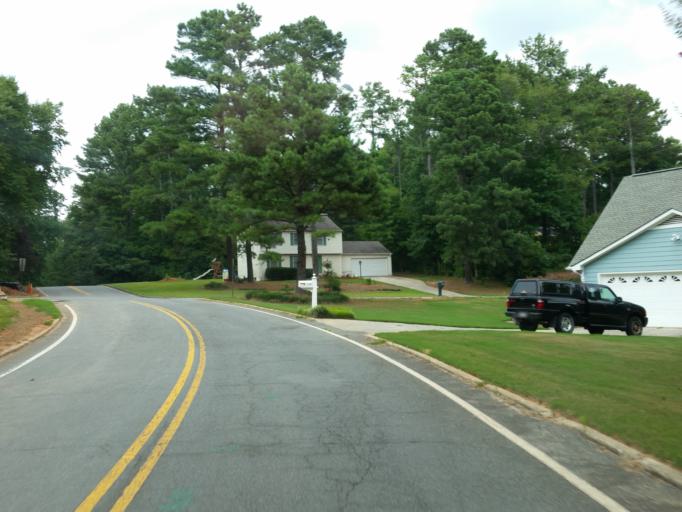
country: US
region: Georgia
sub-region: Fulton County
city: Sandy Springs
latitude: 33.9575
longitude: -84.4538
